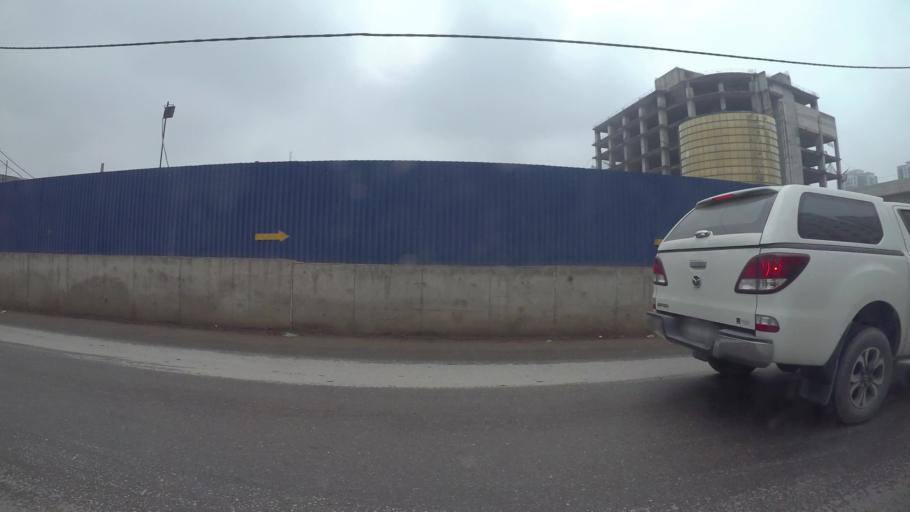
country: VN
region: Ha Noi
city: Cau Dien
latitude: 21.0540
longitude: 105.7817
